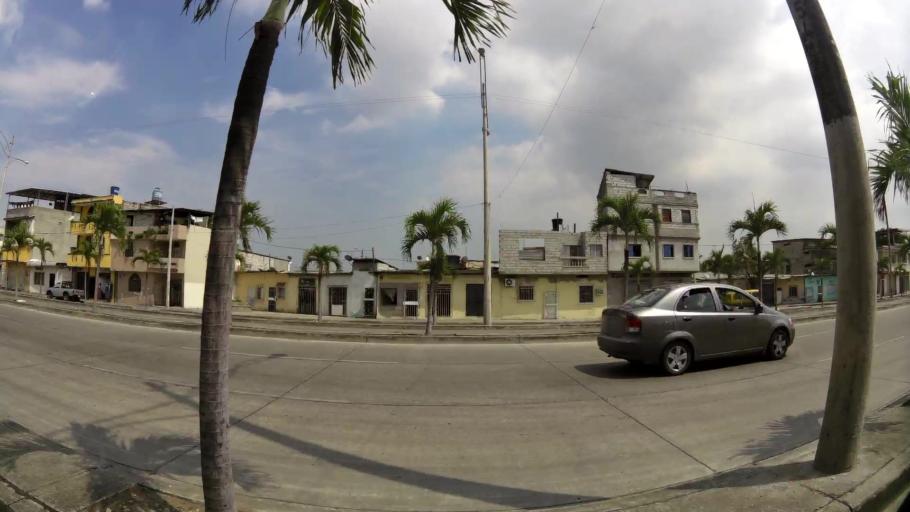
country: EC
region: Guayas
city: Guayaquil
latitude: -2.2557
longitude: -79.8893
